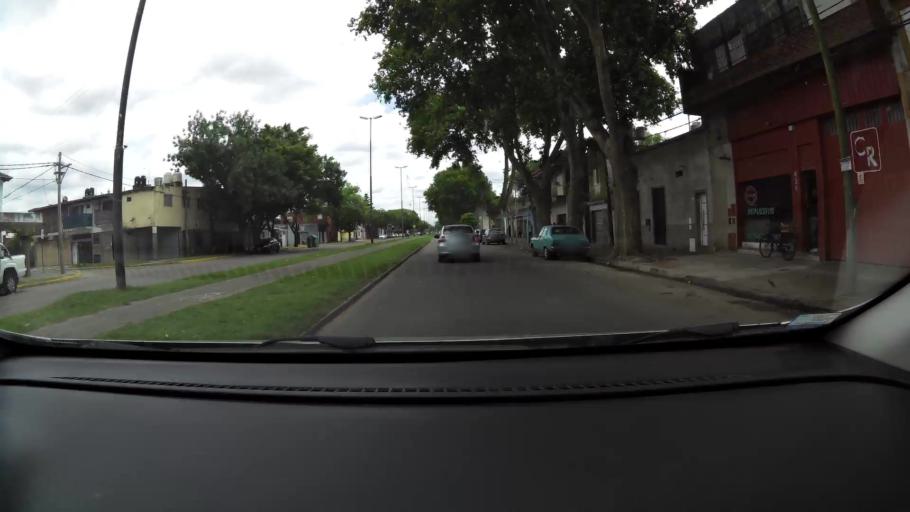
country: AR
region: Santa Fe
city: Gobernador Galvez
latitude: -32.9904
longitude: -60.6395
